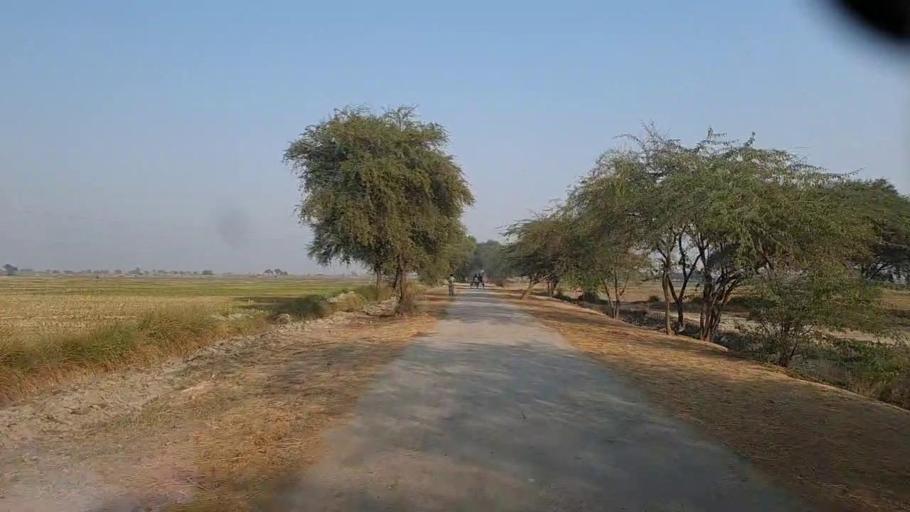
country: PK
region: Sindh
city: Jacobabad
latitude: 28.2398
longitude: 68.4896
